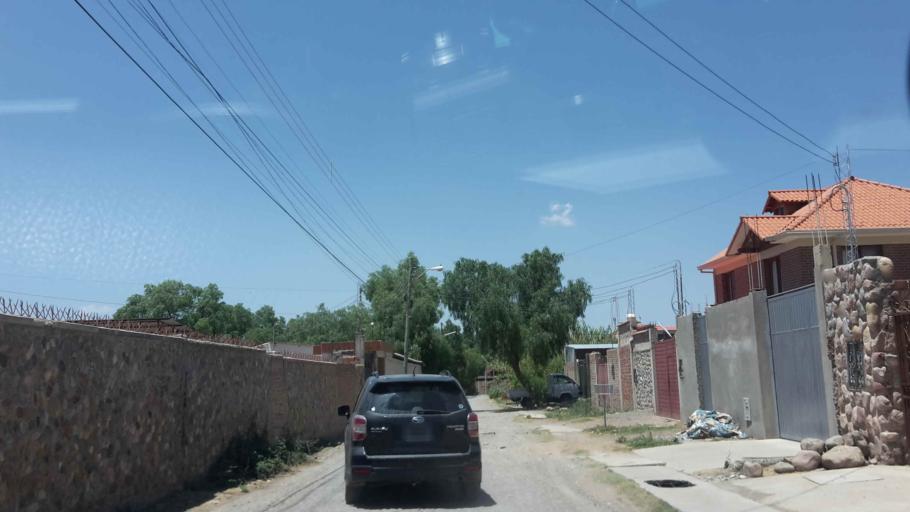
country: BO
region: Cochabamba
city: Cochabamba
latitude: -17.3699
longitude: -66.1957
